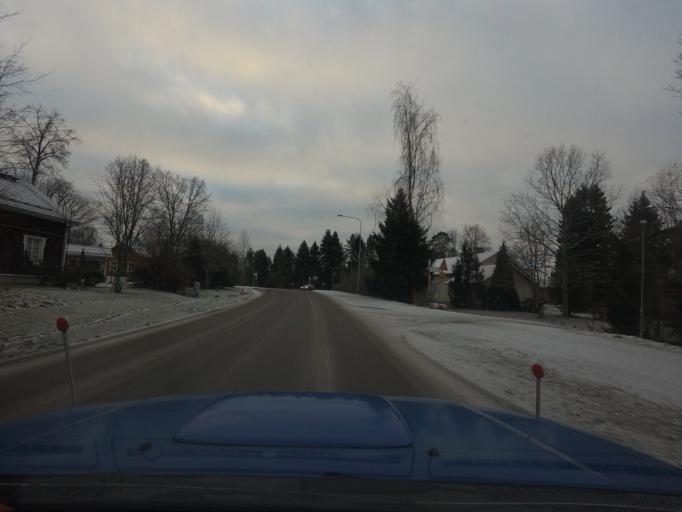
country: FI
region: Uusimaa
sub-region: Helsinki
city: Espoo
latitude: 60.2092
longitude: 24.6419
